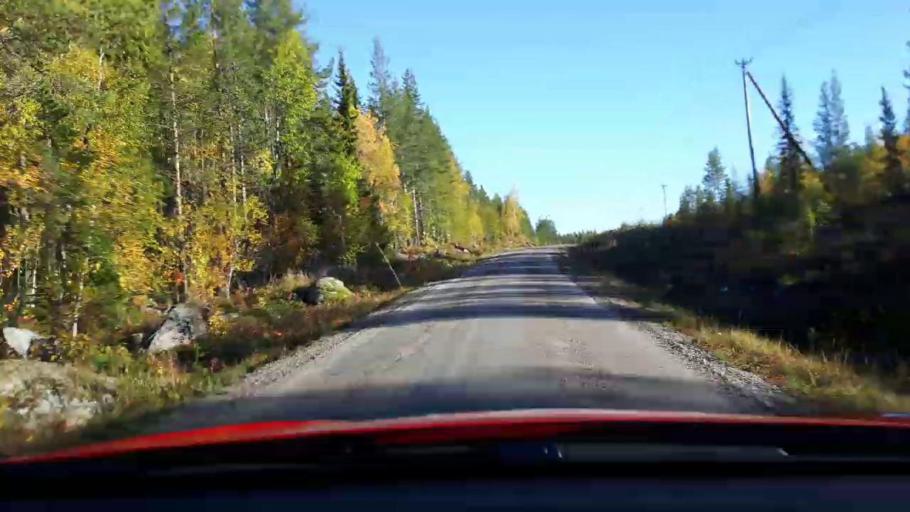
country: SE
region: Jaemtland
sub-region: Stroemsunds Kommun
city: Stroemsund
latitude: 64.3833
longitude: 15.1497
